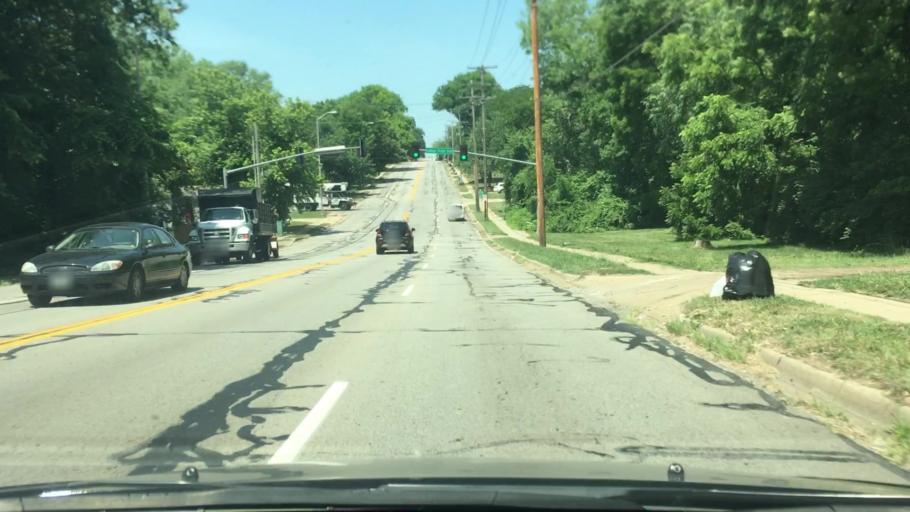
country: US
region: Kansas
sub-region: Johnson County
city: Leawood
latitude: 38.9739
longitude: -94.5863
